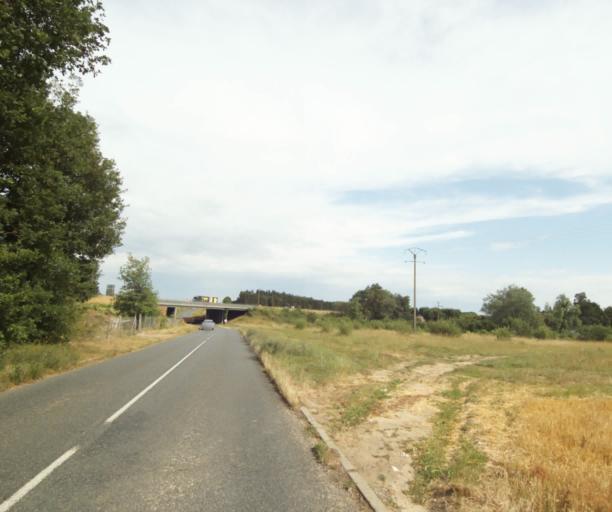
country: FR
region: Ile-de-France
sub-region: Departement de Seine-et-Marne
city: Acheres-la-Foret
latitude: 48.3468
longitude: 2.5871
